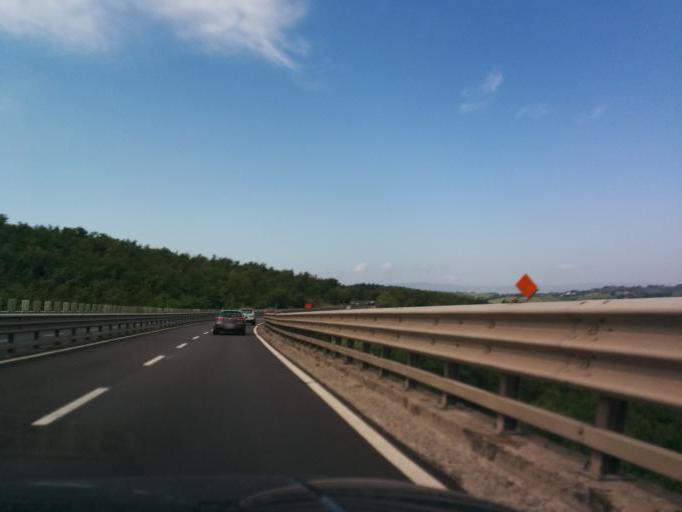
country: IT
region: Tuscany
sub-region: Province of Florence
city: Sambuca
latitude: 43.5323
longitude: 11.2151
